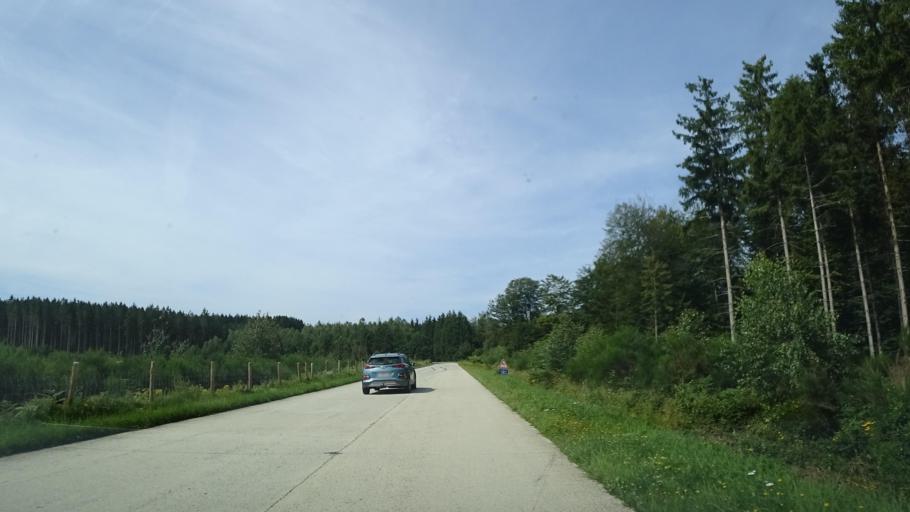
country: BE
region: Wallonia
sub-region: Province du Luxembourg
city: Herbeumont
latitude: 49.8035
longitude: 5.2649
